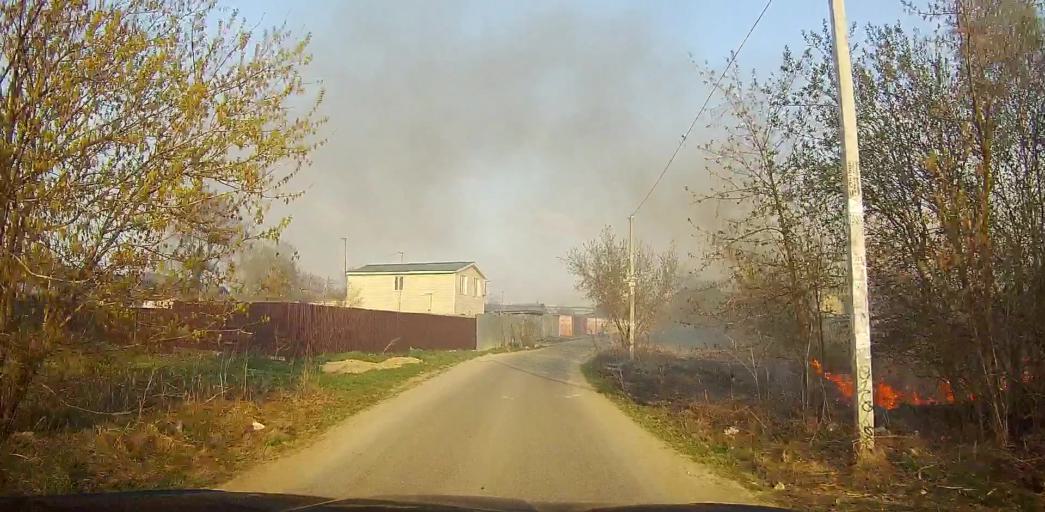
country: RU
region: Moskovskaya
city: Andreyevskoye
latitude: 55.5442
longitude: 37.9725
